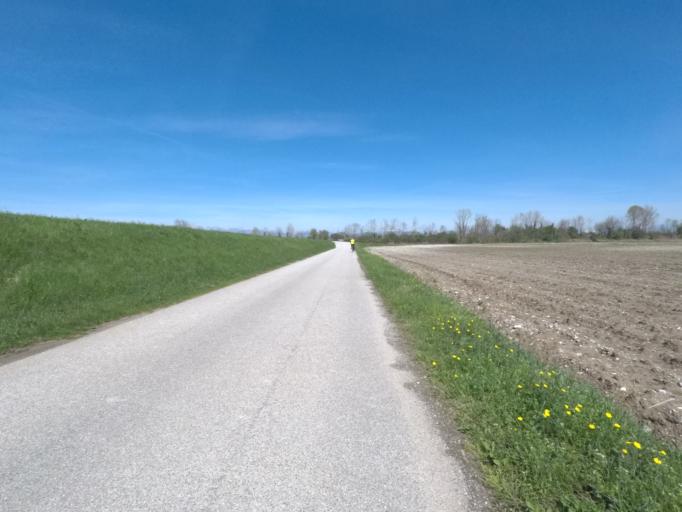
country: IT
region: Friuli Venezia Giulia
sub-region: Provincia di Udine
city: Camino al Tagliamento
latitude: 45.9574
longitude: 12.9130
